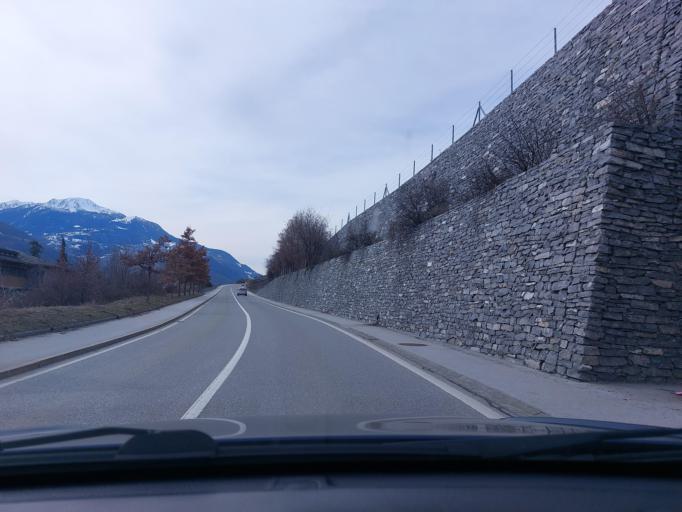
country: CH
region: Valais
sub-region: Sion District
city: Sitten
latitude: 46.2409
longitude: 7.3588
